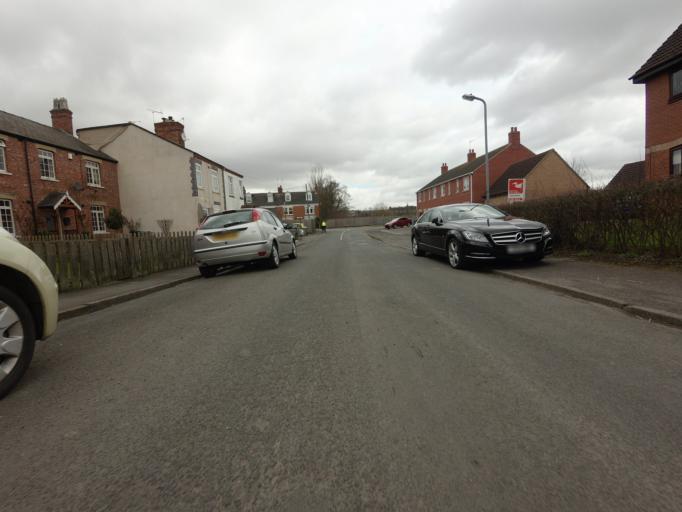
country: GB
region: England
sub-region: Lincolnshire
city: Grantham
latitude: 52.9014
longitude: -0.6326
